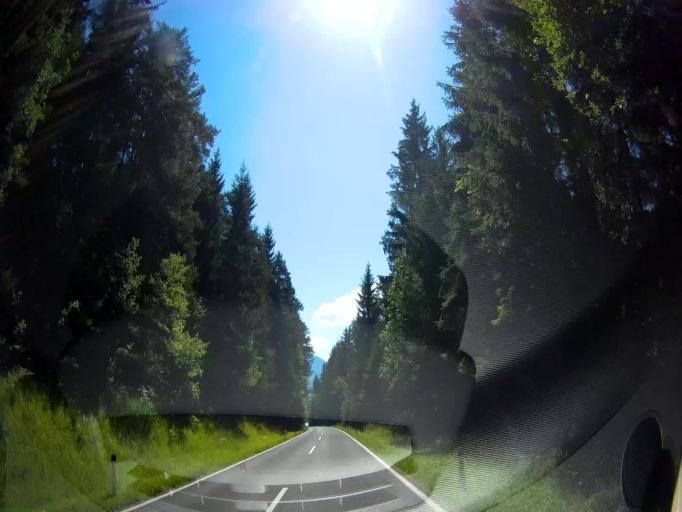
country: AT
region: Carinthia
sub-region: Politischer Bezirk Volkermarkt
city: Gallizien
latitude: 46.5433
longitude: 14.5436
